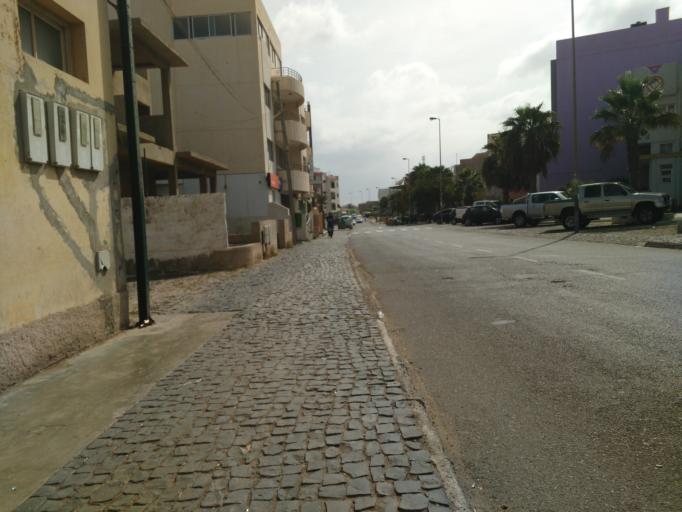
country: CV
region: Sal
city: Espargos
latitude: 16.7554
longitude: -22.9411
